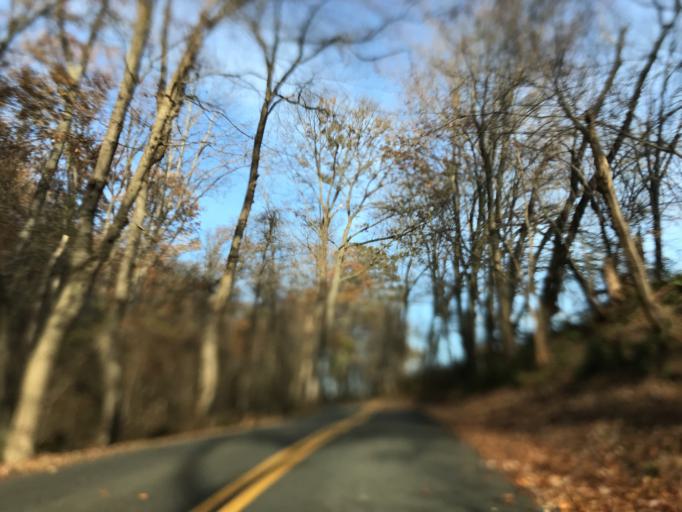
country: US
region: Maryland
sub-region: Carroll County
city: Hampstead
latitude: 39.5663
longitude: -76.7897
